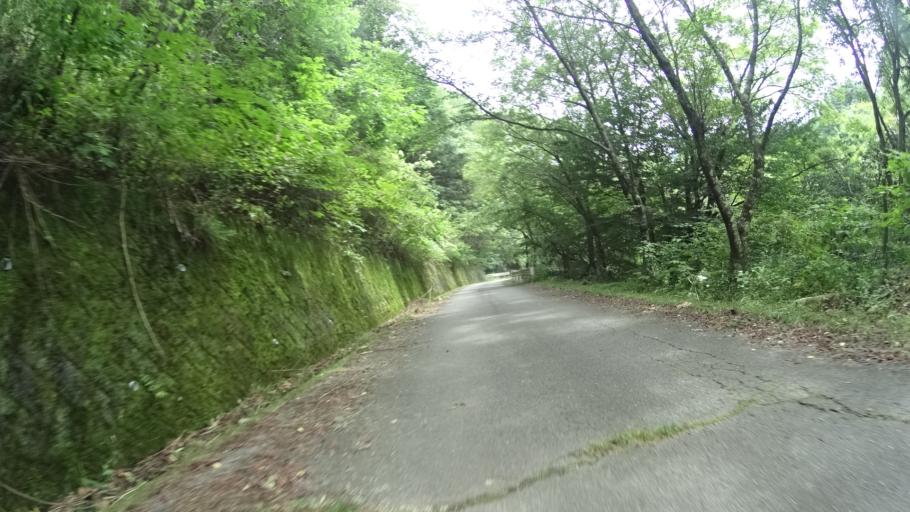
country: JP
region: Yamanashi
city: Kofu-shi
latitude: 35.8263
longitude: 138.5957
